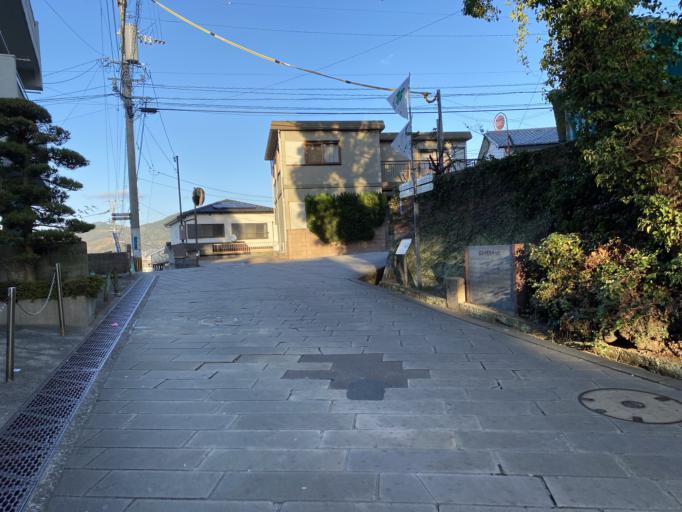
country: JP
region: Nagasaki
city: Nagasaki-shi
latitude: 32.7385
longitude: 129.8742
